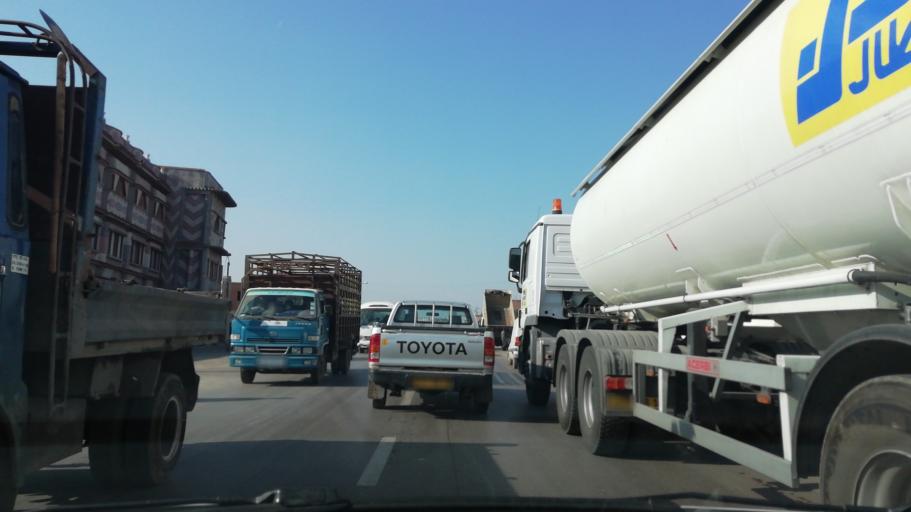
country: DZ
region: Mostaganem
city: Mostaganem
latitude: 35.7402
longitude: -0.0271
